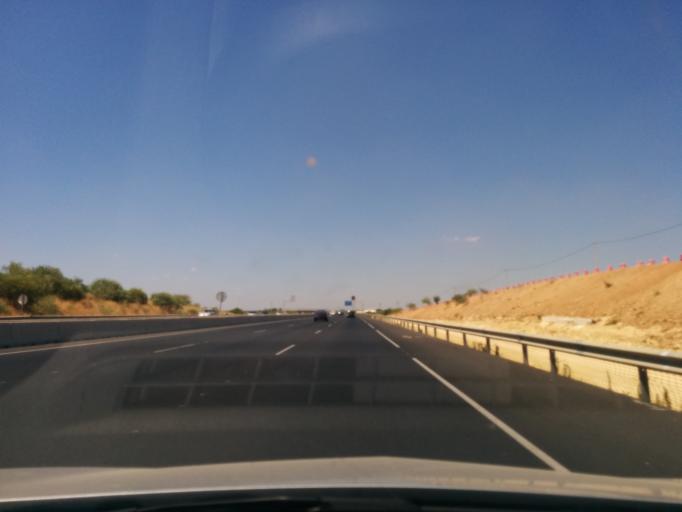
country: ES
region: Andalusia
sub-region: Provincia de Sevilla
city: Espartinas
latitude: 37.3642
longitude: -6.1227
